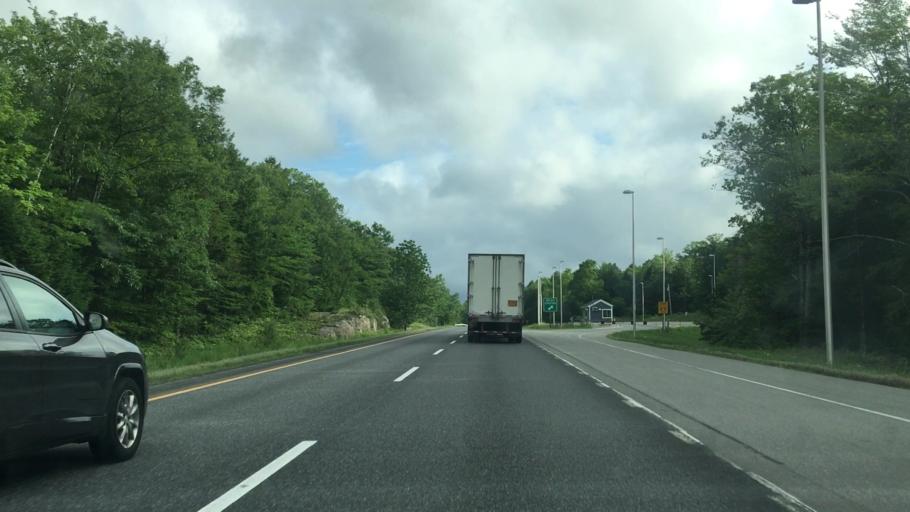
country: US
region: Maine
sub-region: Kennebec County
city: Sidney
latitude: 44.4050
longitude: -69.7506
